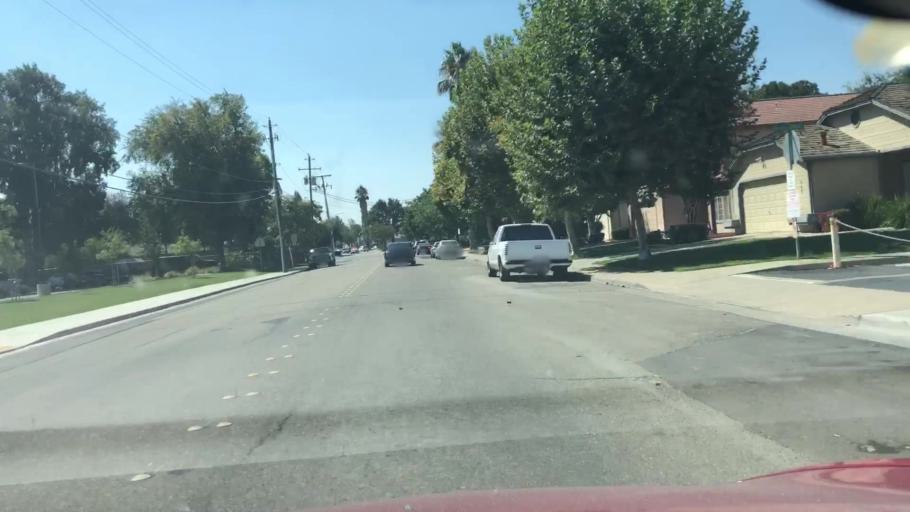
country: US
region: California
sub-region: San Joaquin County
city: Tracy
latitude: 37.7289
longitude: -121.4332
